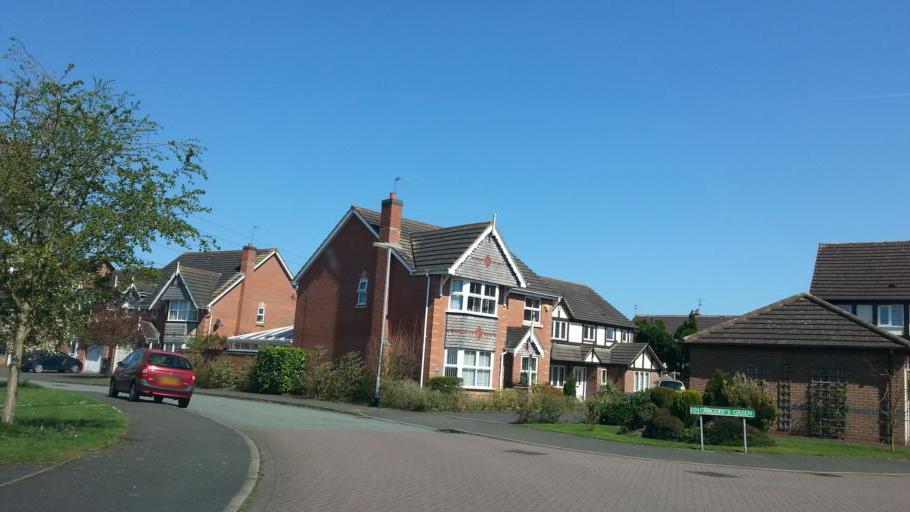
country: GB
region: England
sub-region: Staffordshire
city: Brewood
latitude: 52.6619
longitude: -2.1417
